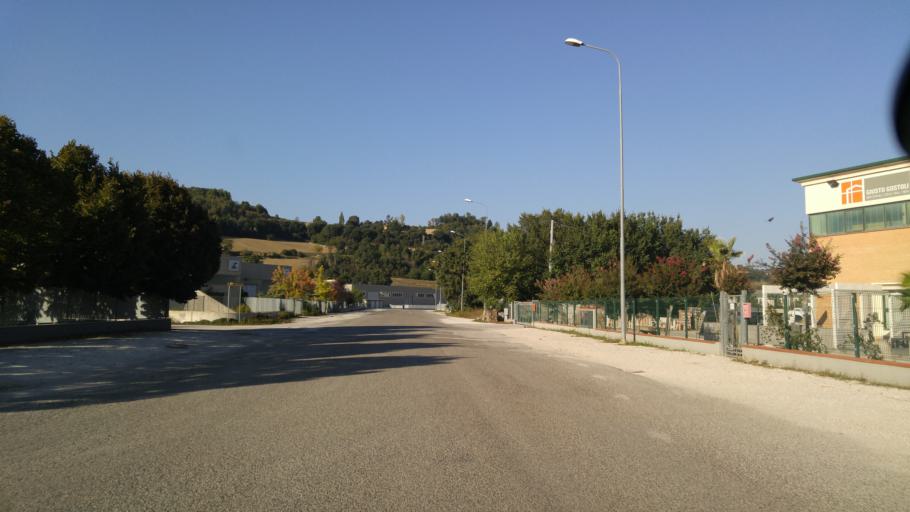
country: IT
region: The Marches
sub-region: Provincia di Pesaro e Urbino
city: Fermignano
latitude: 43.6917
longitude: 12.6487
